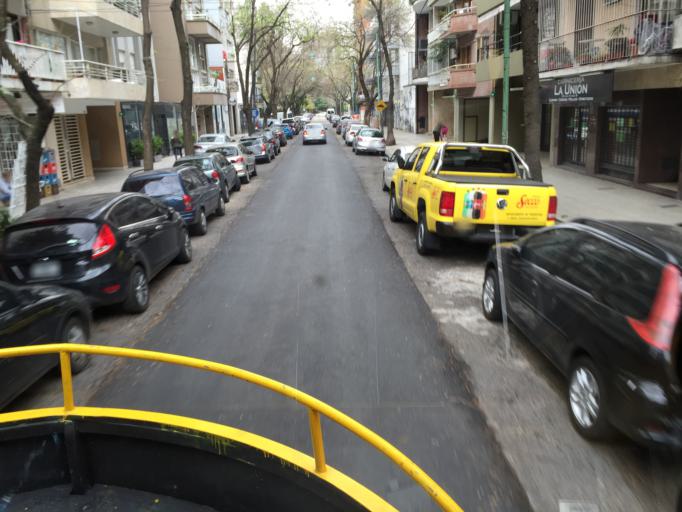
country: AR
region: Buenos Aires F.D.
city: Colegiales
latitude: -34.5702
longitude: -58.4341
